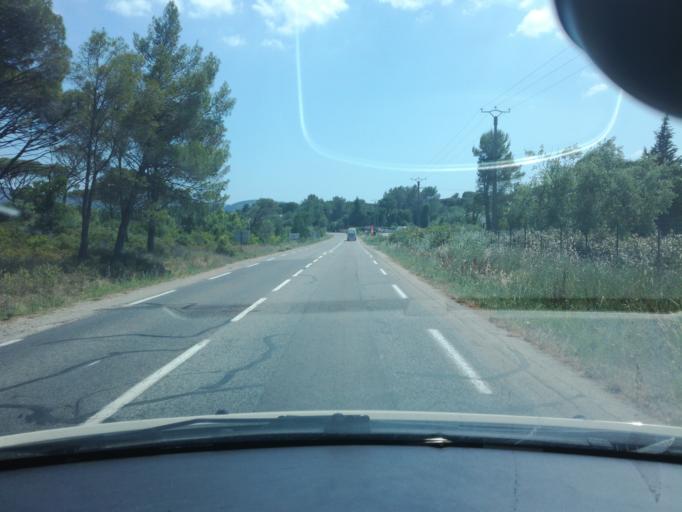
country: FR
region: Provence-Alpes-Cote d'Azur
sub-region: Departement du Var
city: Le Muy
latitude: 43.4909
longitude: 6.5652
